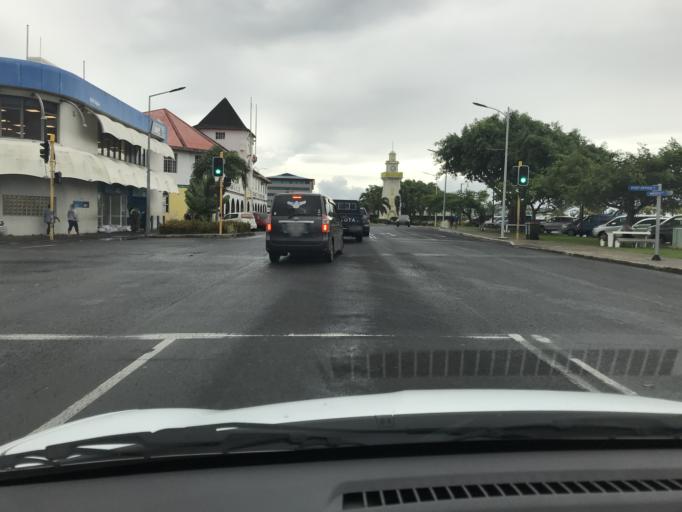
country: WS
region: Tuamasaga
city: Apia
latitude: -13.8310
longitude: -171.7675
